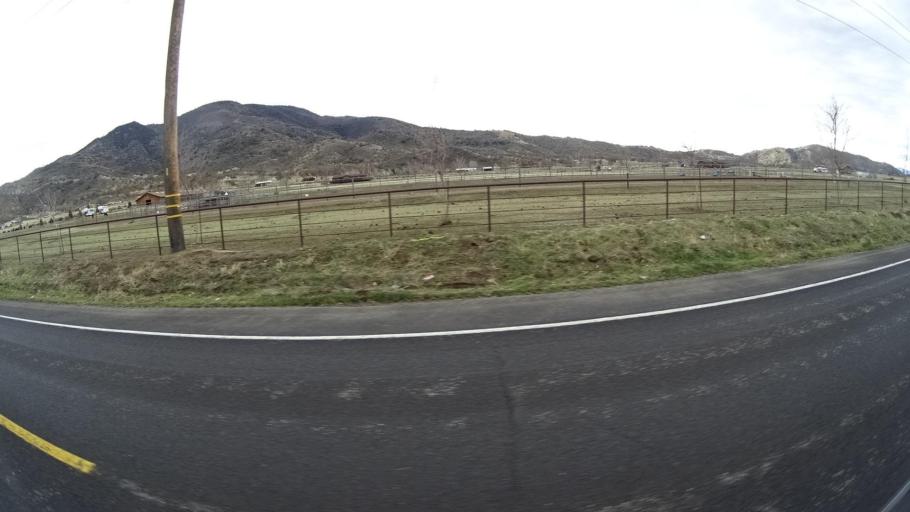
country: US
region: California
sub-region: Kern County
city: Stallion Springs
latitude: 35.0954
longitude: -118.6082
